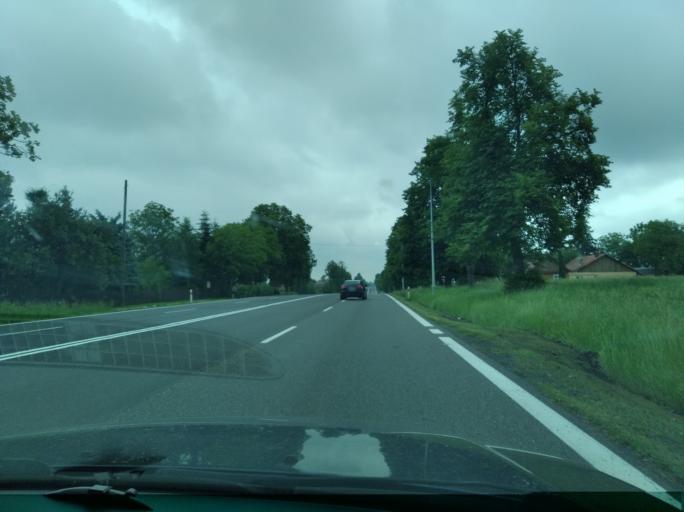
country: PL
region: Subcarpathian Voivodeship
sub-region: Powiat przeworski
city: Grzeska
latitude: 50.0625
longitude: 22.4548
